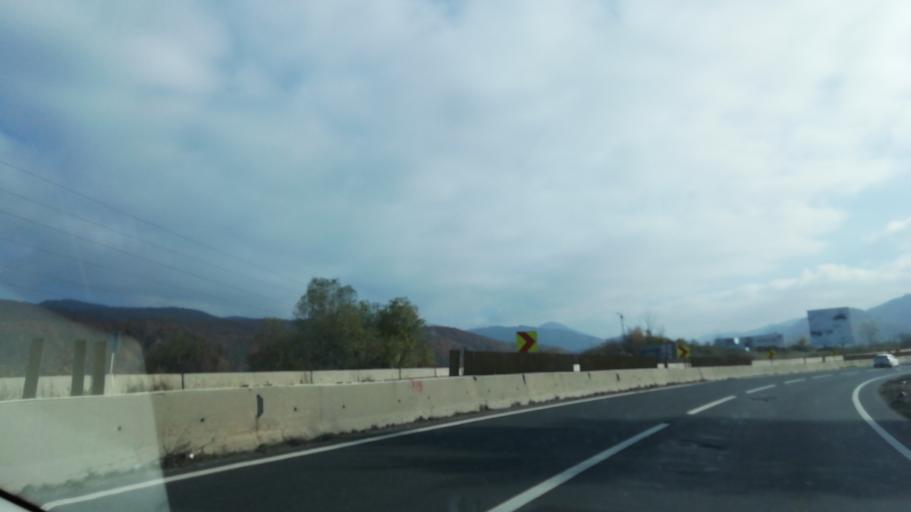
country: TR
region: Duzce
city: Kaynasli
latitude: 40.7710
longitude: 31.3537
